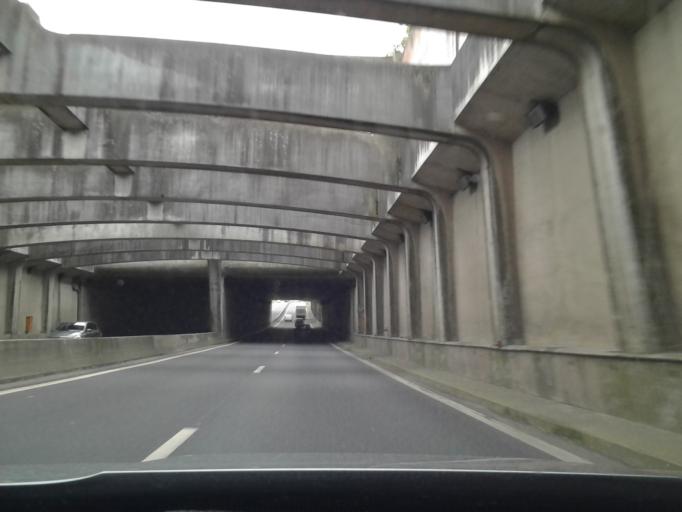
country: FR
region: Lower Normandy
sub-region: Departement de la Manche
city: Saint-Hilaire-Petitville
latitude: 49.3147
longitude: -1.2313
